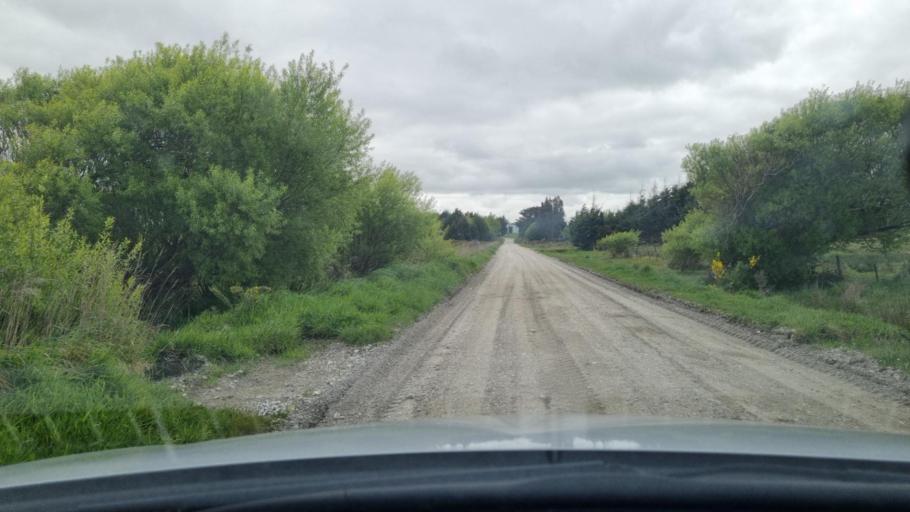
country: NZ
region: Southland
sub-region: Invercargill City
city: Invercargill
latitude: -46.4355
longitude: 168.3896
